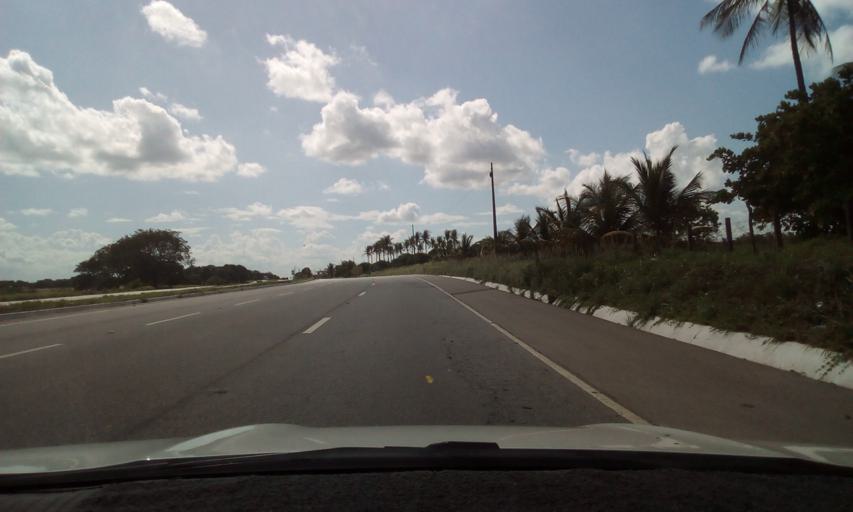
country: BR
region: Paraiba
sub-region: Pilar
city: Pilar
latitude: -7.1882
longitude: -35.2807
